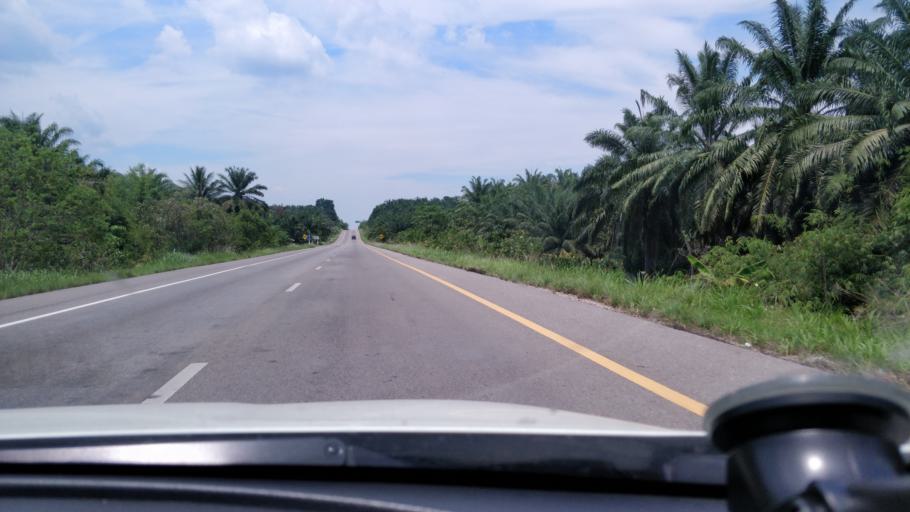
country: TH
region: Krabi
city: Plai Phraya
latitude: 8.5451
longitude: 98.9087
